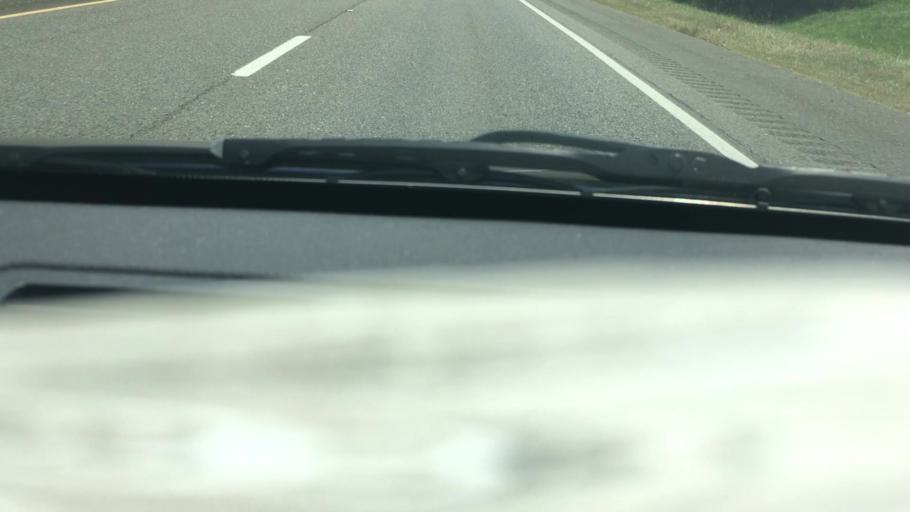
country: US
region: Alabama
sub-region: Pickens County
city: Gordo
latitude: 33.2793
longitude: -87.7834
